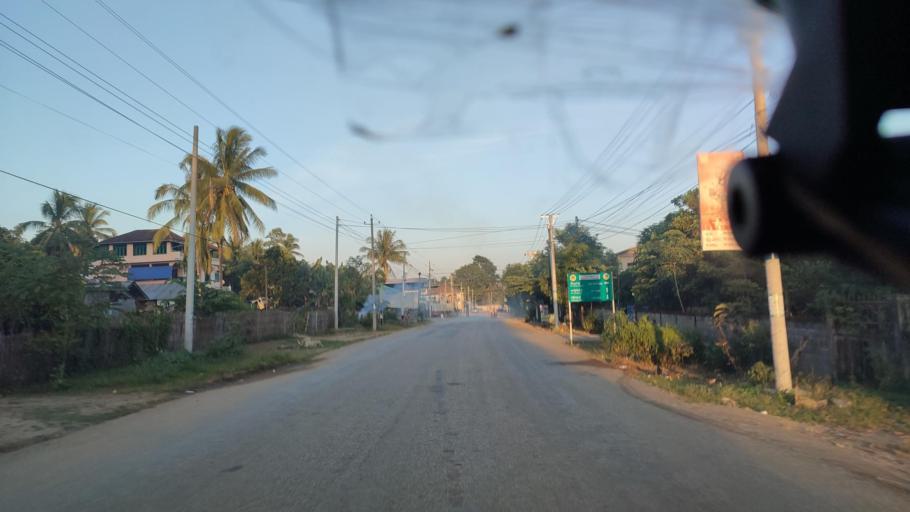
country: TH
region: Chiang Rai
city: Mae Sai
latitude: 20.8697
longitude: 99.9070
